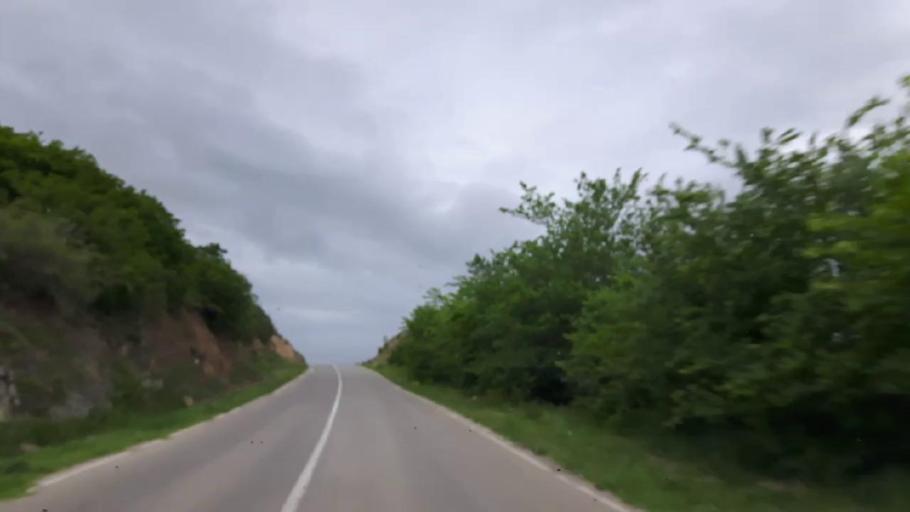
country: GE
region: Shida Kartli
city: Gori
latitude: 41.9901
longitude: 44.0398
